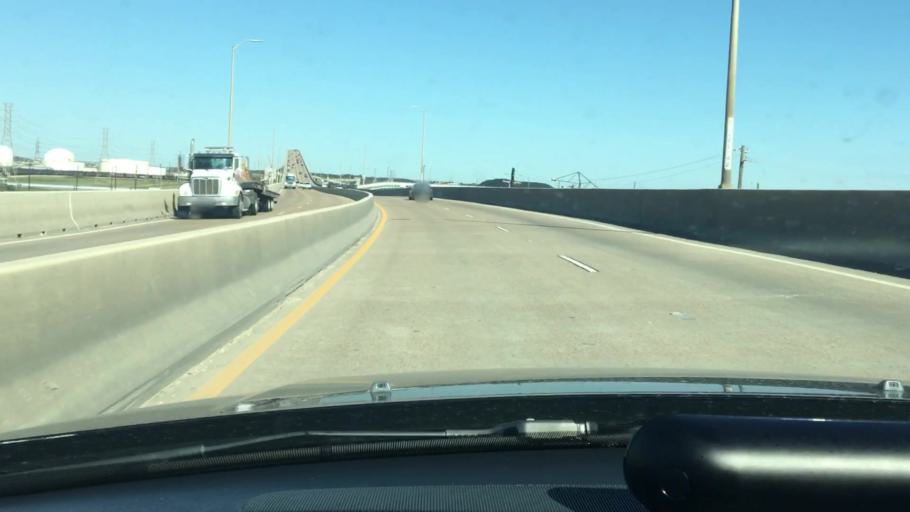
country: US
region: Texas
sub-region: Harris County
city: Deer Park
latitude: 29.7216
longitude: -95.1479
